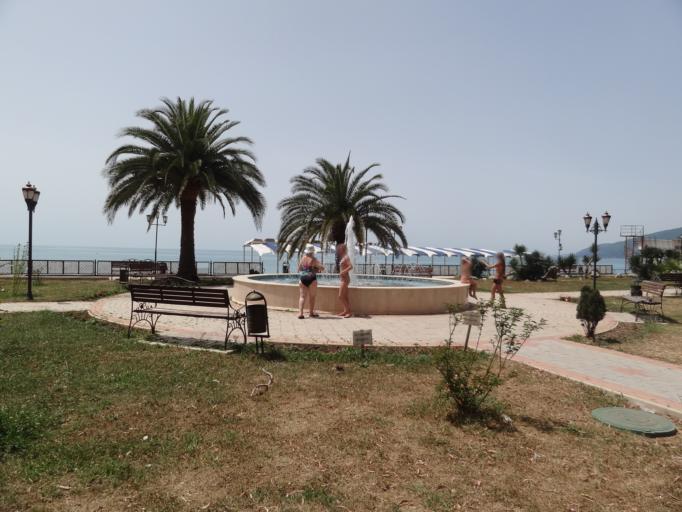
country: GE
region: Abkhazia
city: Gagra
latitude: 43.2946
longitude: 40.2589
